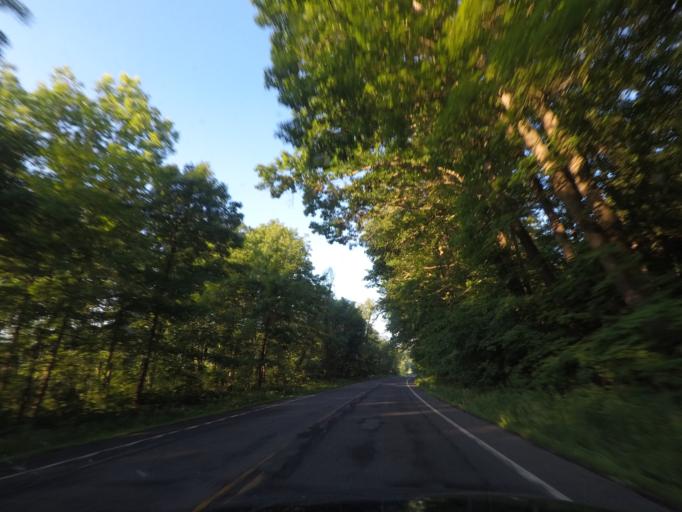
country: US
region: New York
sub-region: Dutchess County
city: Pine Plains
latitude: 41.9805
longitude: -73.5226
